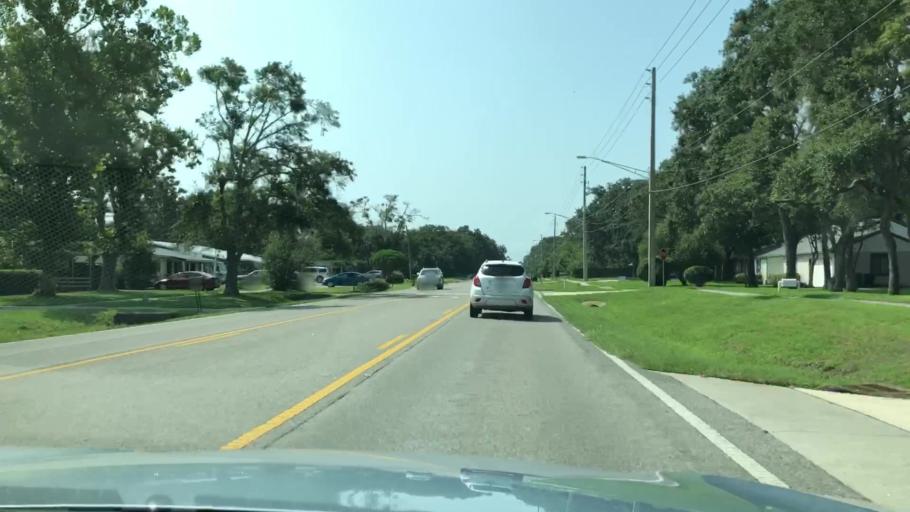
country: US
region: Florida
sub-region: Duval County
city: Neptune Beach
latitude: 30.3214
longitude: -81.4087
